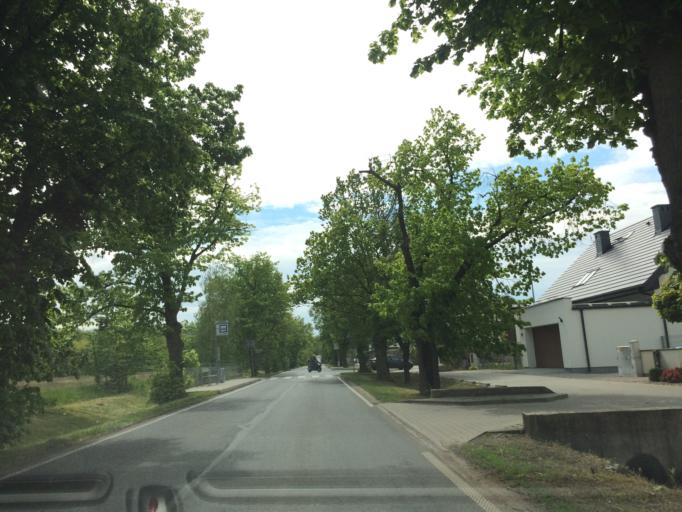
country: PL
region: Lower Silesian Voivodeship
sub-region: Powiat wroclawski
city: Smolec
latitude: 51.1607
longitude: 16.8775
